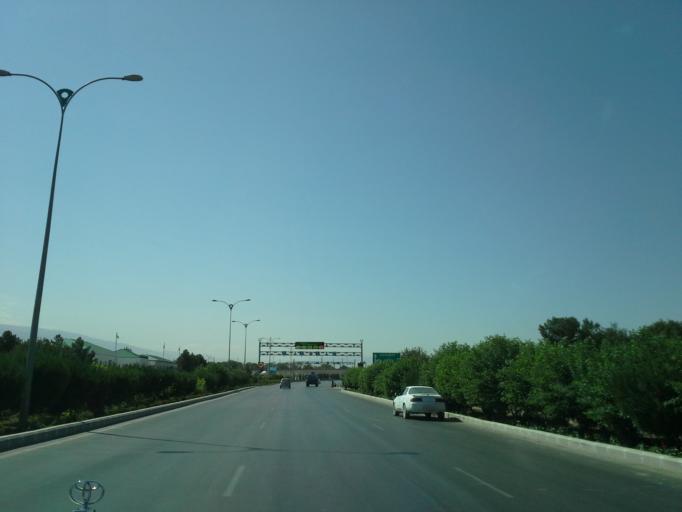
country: TM
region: Ahal
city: Annau
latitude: 37.9116
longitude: 58.4923
